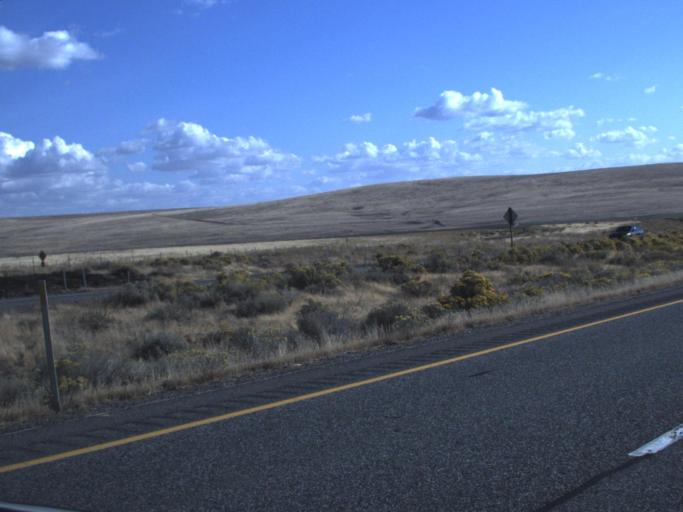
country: US
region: Washington
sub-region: Benton County
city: Highland
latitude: 46.0294
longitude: -119.2249
